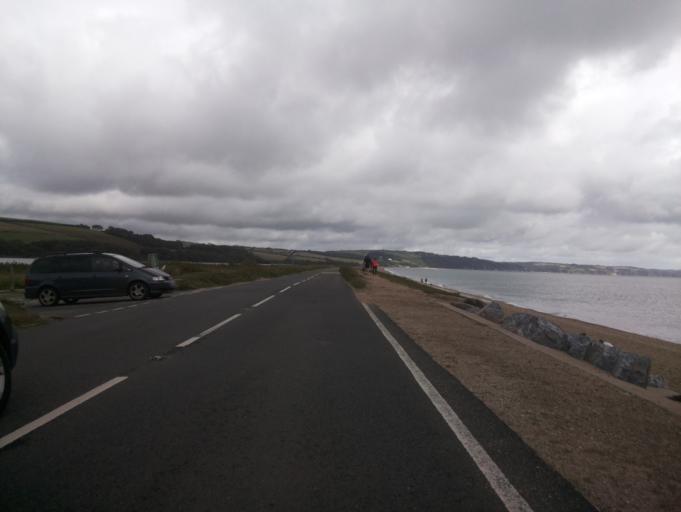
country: GB
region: England
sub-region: Devon
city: Dartmouth
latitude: 50.2695
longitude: -3.6517
